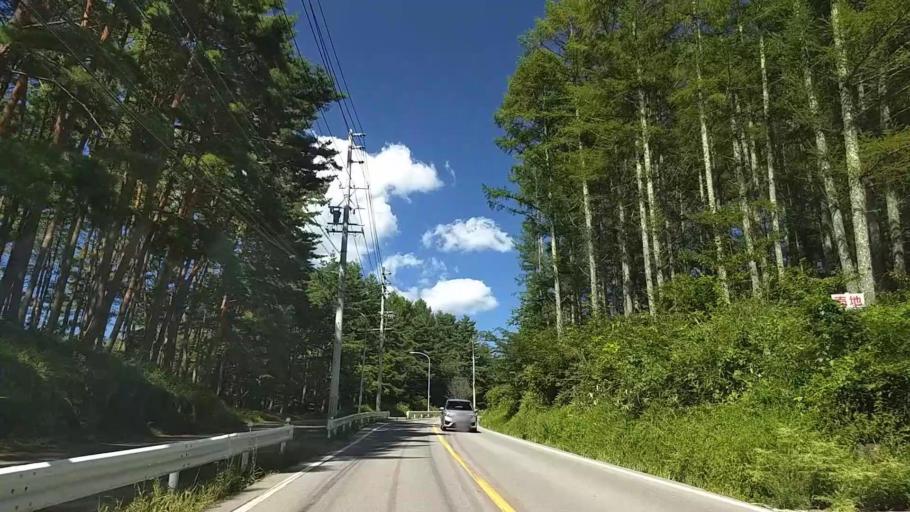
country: JP
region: Nagano
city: Chino
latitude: 36.0352
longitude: 138.2374
